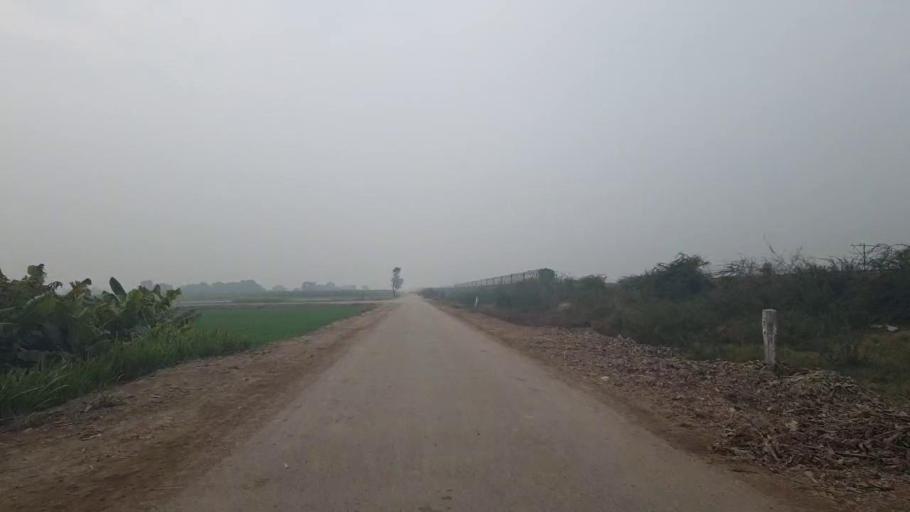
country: PK
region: Sindh
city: Tando Adam
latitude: 25.7049
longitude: 68.6416
